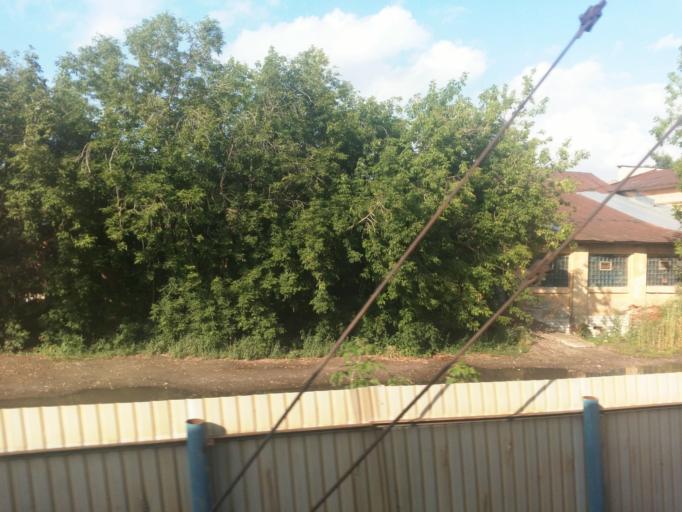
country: RU
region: Tatarstan
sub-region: Gorod Kazan'
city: Kazan
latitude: 55.8047
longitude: 49.0590
